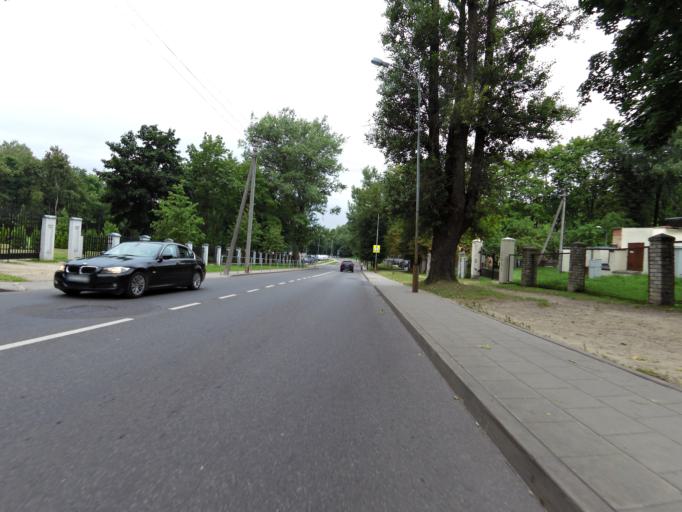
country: LT
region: Vilnius County
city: Rasos
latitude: 54.6668
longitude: 25.2980
